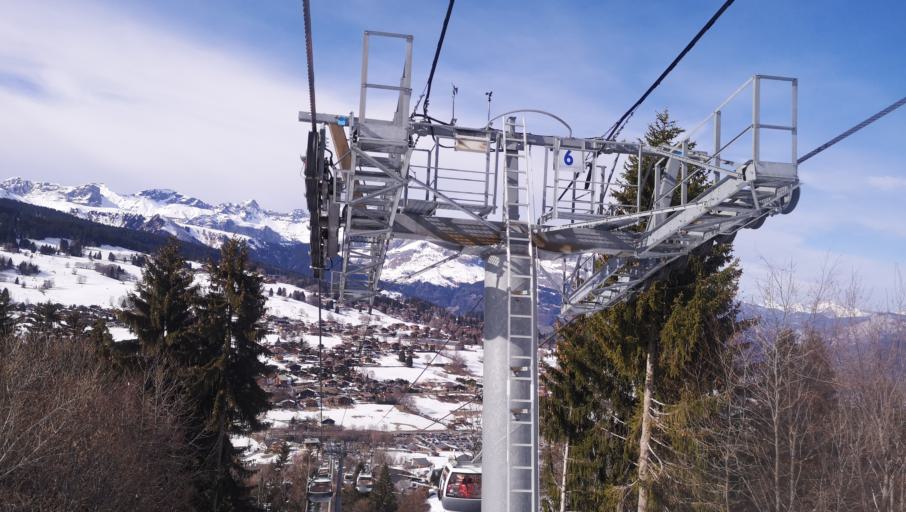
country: FR
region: Rhone-Alpes
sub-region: Departement de la Haute-Savoie
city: Combloux
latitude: 45.8757
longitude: 6.6467
